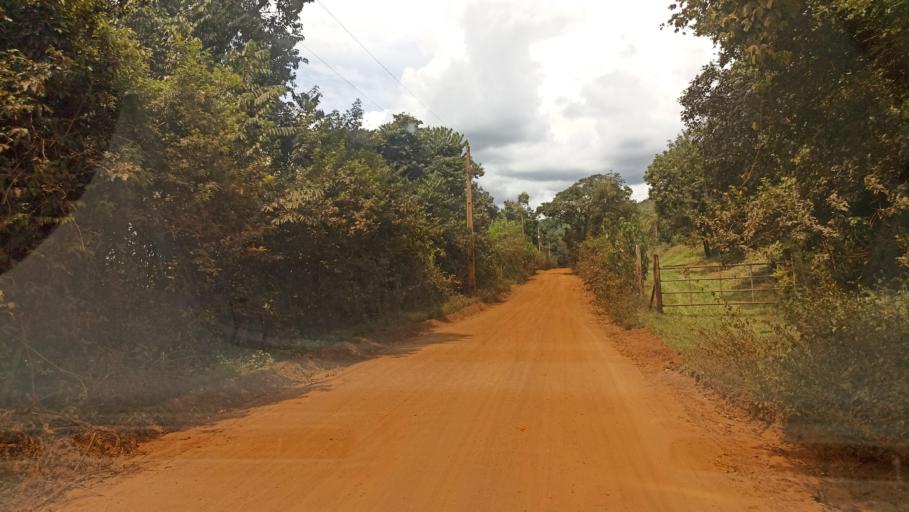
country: BR
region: Minas Gerais
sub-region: Itabirito
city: Itabirito
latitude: -20.3357
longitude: -43.7684
